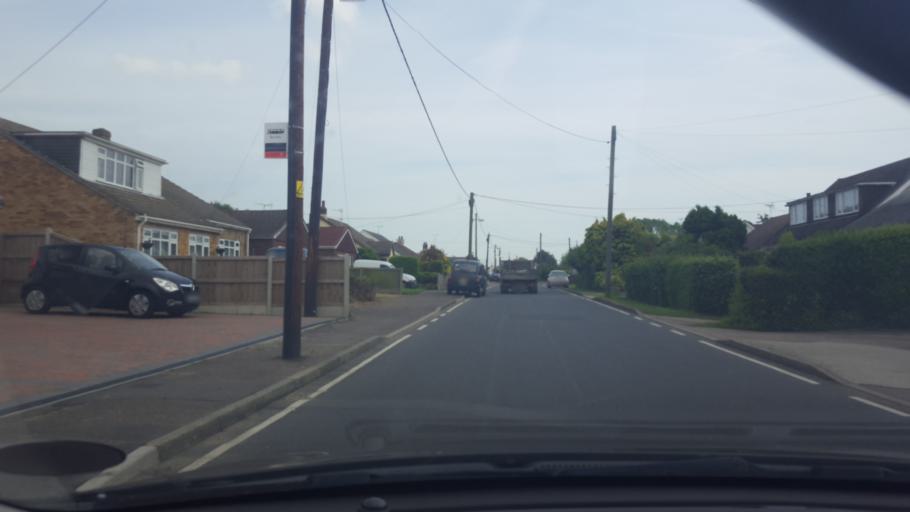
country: GB
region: England
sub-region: Essex
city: Little Clacton
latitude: 51.8256
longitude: 1.1441
